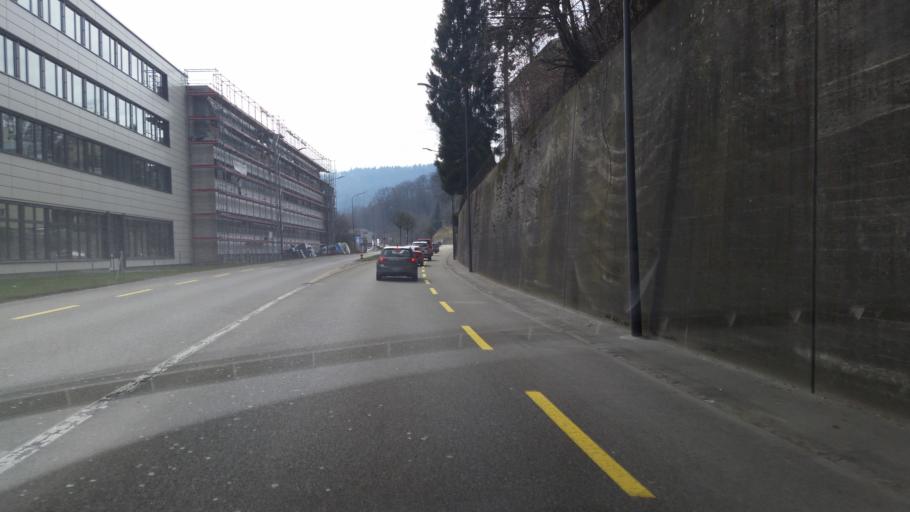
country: CH
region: Aargau
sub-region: Bezirk Baden
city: Baden
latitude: 47.4643
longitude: 8.3071
